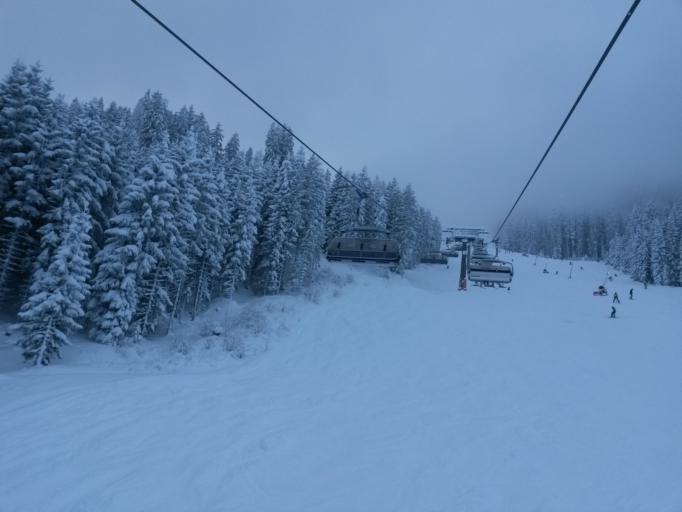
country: AT
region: Salzburg
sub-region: Politischer Bezirk Sankt Johann im Pongau
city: Dorfgastein
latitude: 47.2400
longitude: 13.1797
